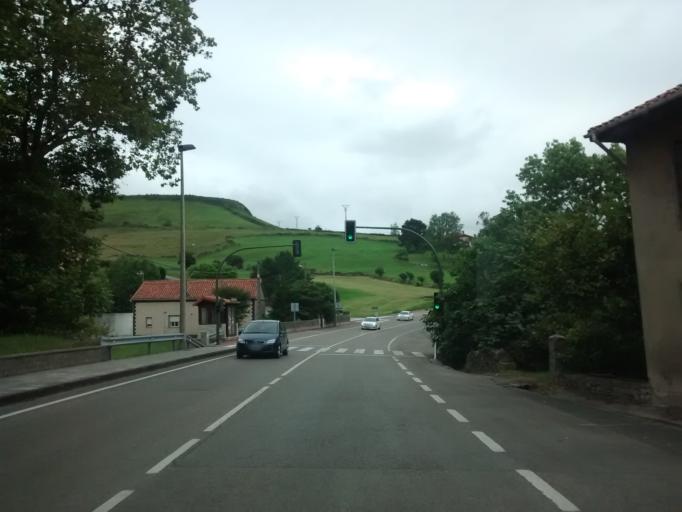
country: ES
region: Cantabria
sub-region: Provincia de Cantabria
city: Suances
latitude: 43.4077
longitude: -4.0427
